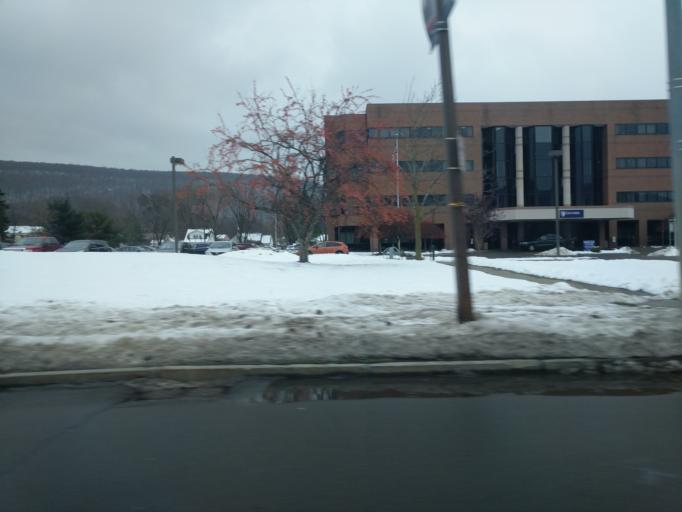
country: US
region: New York
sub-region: Steuben County
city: Corning
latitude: 42.1490
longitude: -77.0529
